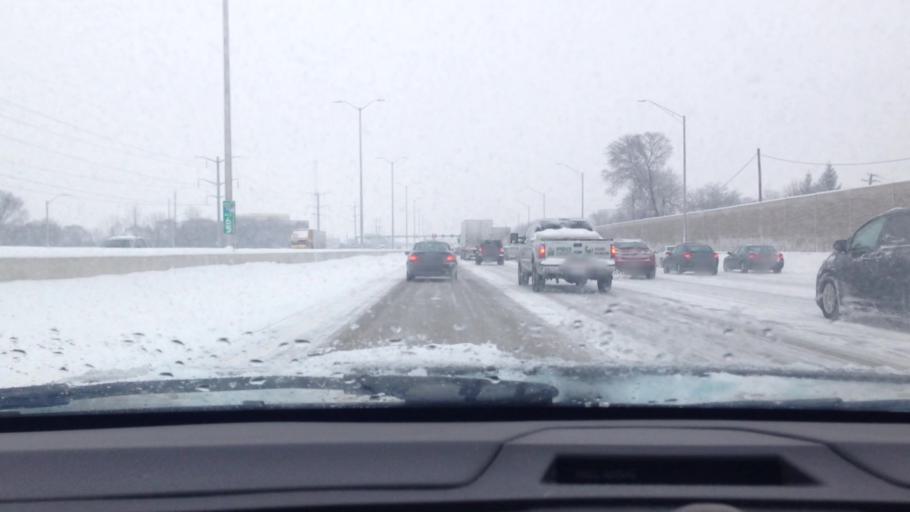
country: US
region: Illinois
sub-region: Cook County
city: Hoffman Estates
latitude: 42.0628
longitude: -88.0943
